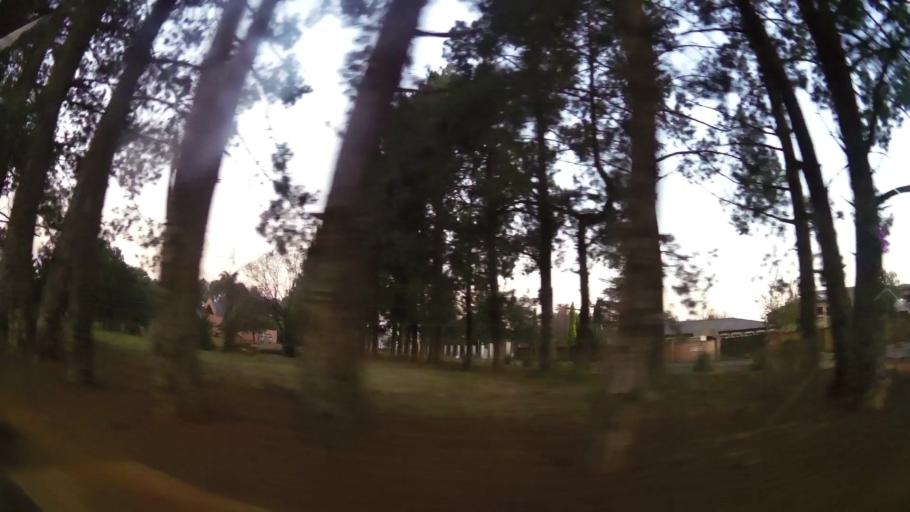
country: ZA
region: Gauteng
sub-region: City of Tshwane Metropolitan Municipality
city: Centurion
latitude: -25.8473
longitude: 28.1153
